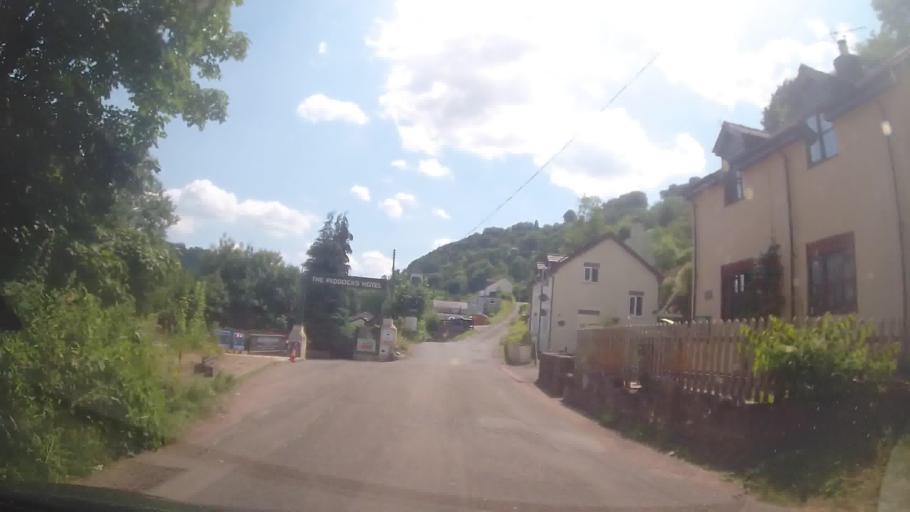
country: GB
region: England
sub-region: Herefordshire
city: Whitchurch
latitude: 51.8468
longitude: -2.6464
